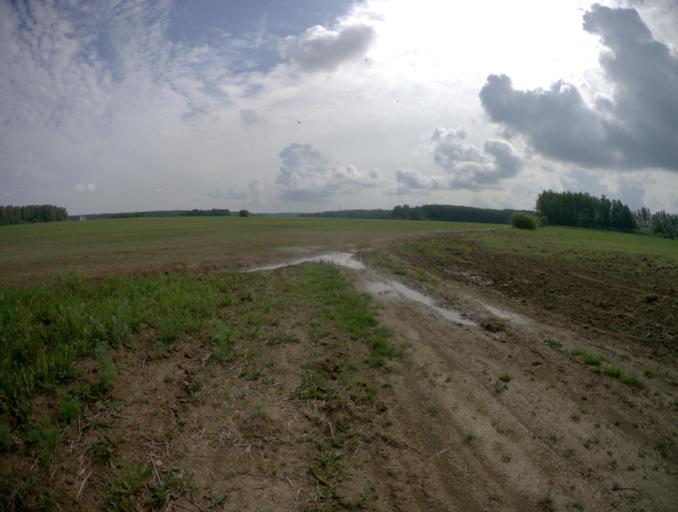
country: RU
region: Vladimir
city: Lakinsk
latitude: 56.0966
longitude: 39.9132
